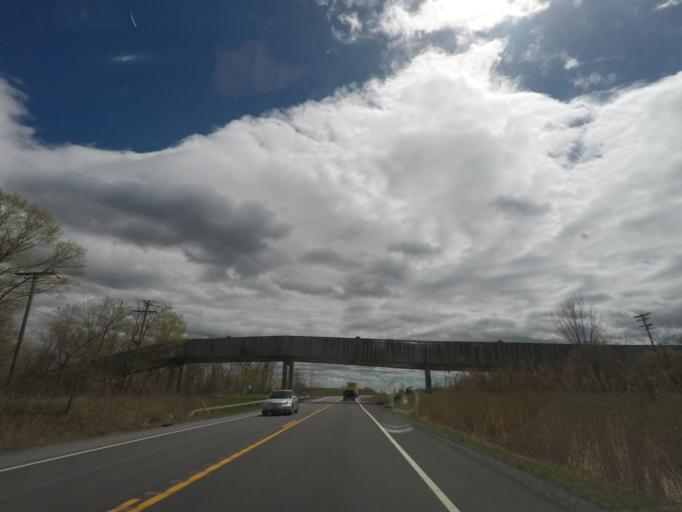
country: US
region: New York
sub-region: Albany County
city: Ravena
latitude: 42.4911
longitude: -73.7932
